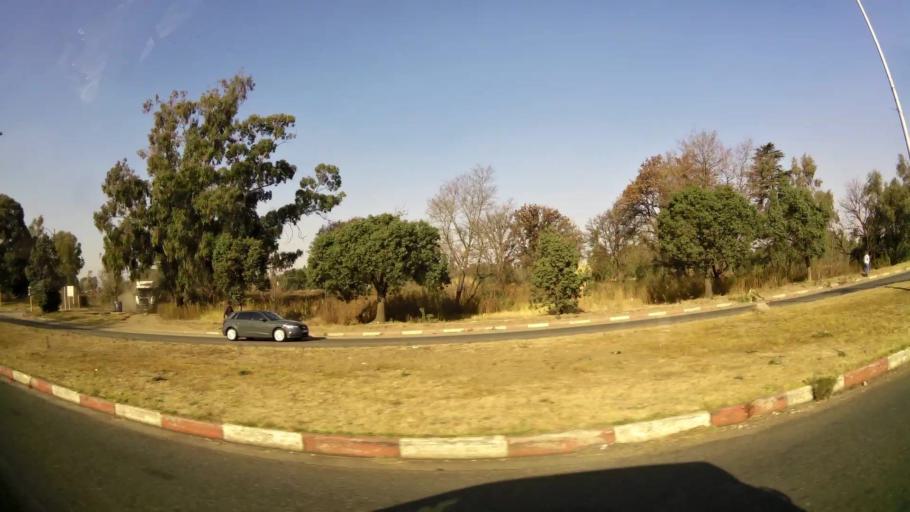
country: ZA
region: Gauteng
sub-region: West Rand District Municipality
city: Randfontein
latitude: -26.1603
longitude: 27.7147
